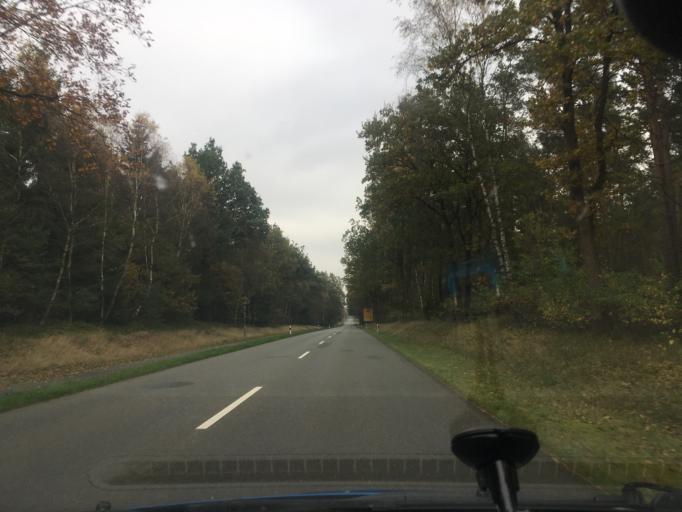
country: DE
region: Lower Saxony
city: Bispingen
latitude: 53.0670
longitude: 9.9653
